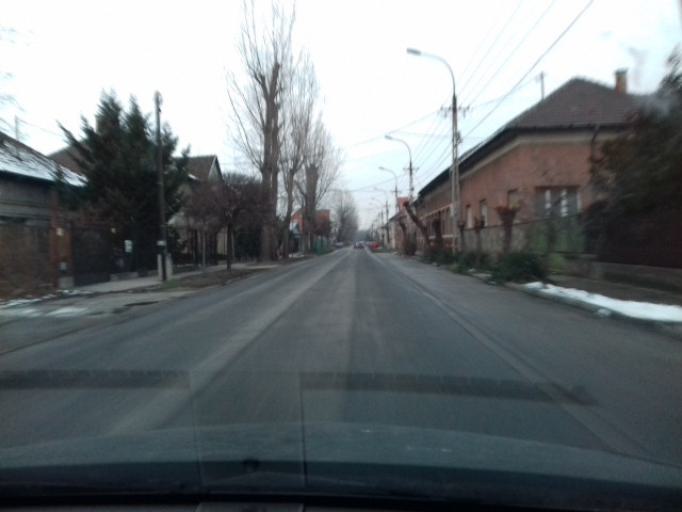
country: HU
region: Budapest
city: Budapest XV. keruelet
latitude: 47.5572
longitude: 19.1101
